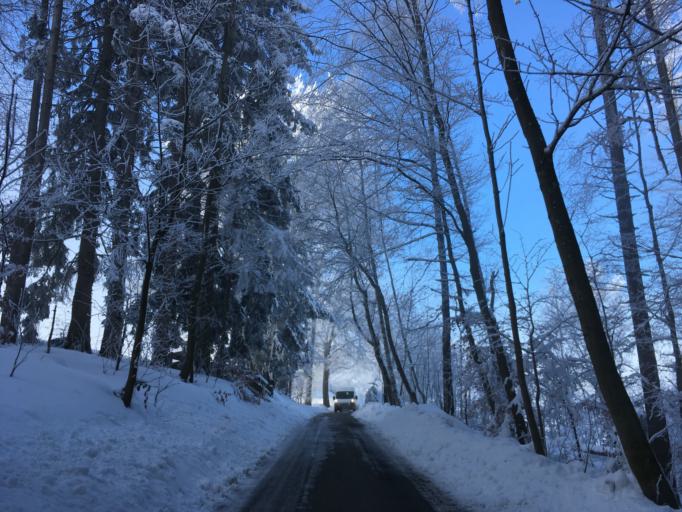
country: DE
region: Bavaria
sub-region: Upper Bavaria
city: Rimsting
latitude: 47.8839
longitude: 12.3168
